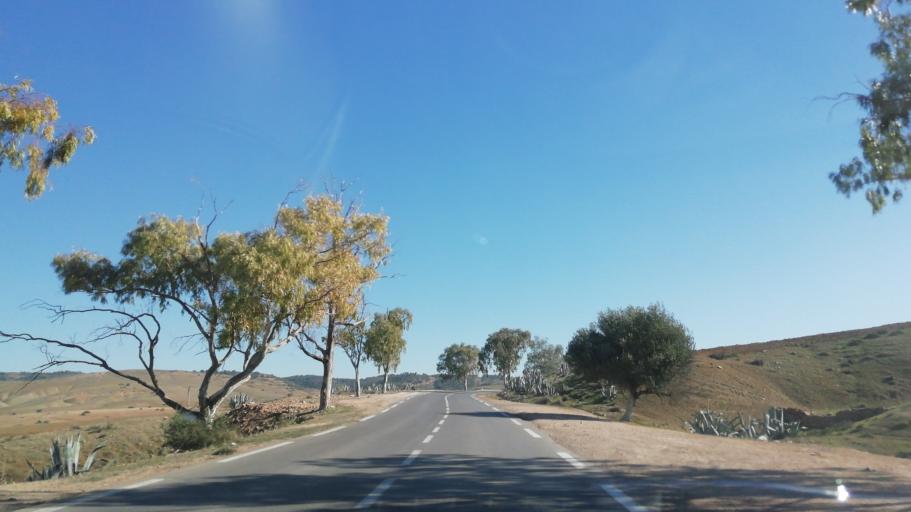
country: DZ
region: Tlemcen
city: Nedroma
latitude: 34.8282
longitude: -1.6418
